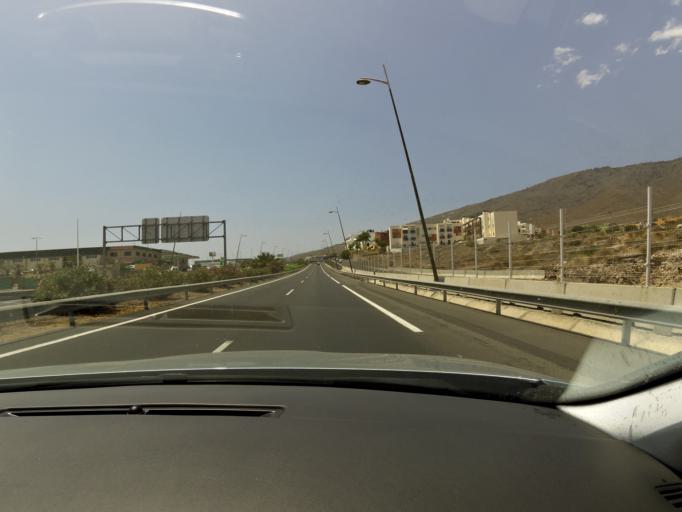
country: ES
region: Canary Islands
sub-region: Provincia de Santa Cruz de Tenerife
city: Adeje
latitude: 28.1174
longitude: -16.7372
